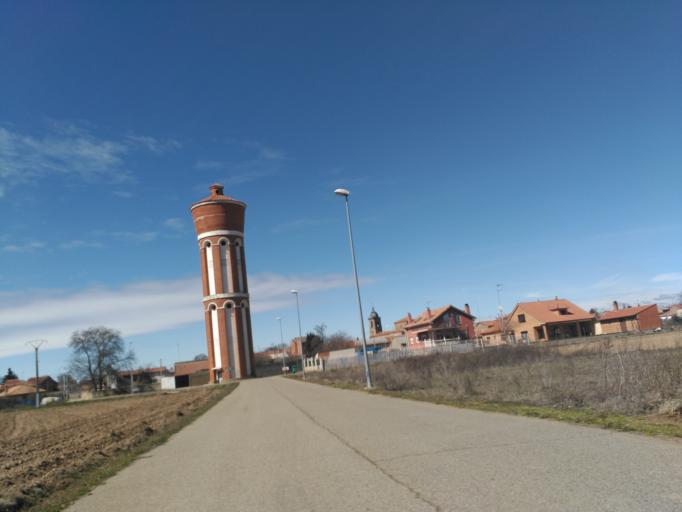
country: ES
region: Castille and Leon
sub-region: Provincia de Leon
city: Hospital de Orbigo
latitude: 42.4406
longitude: -5.8792
